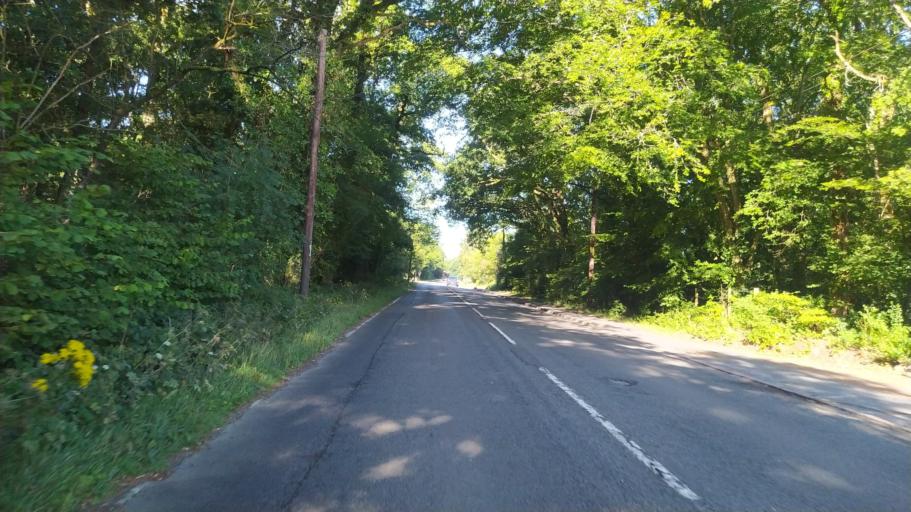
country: GB
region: England
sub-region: Hampshire
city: Cadnam
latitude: 50.9148
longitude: -1.5474
